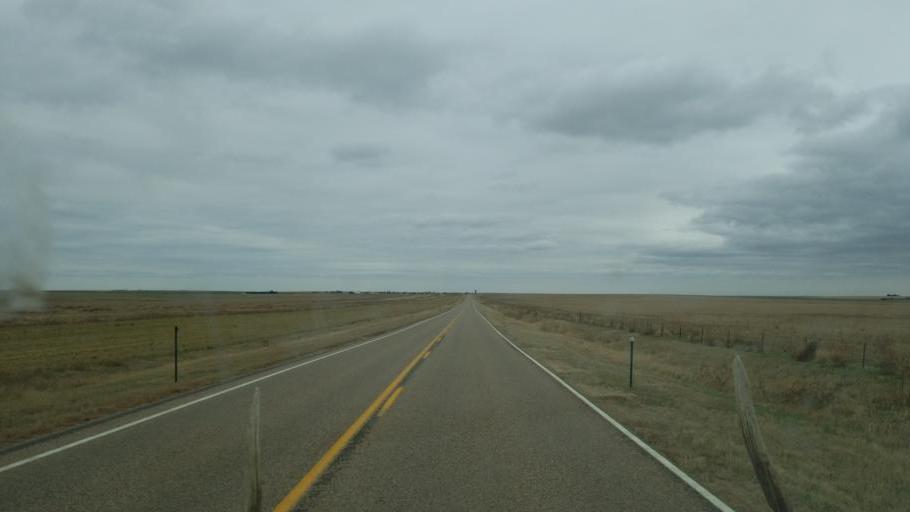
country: US
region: Colorado
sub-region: Cheyenne County
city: Cheyenne Wells
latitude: 38.8532
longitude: -102.2187
